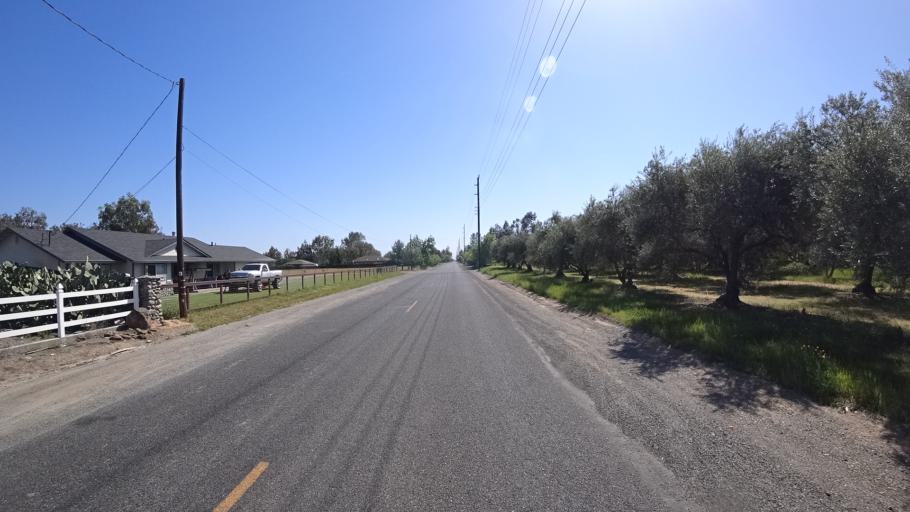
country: US
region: California
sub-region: Glenn County
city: Orland
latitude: 39.7256
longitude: -122.1862
